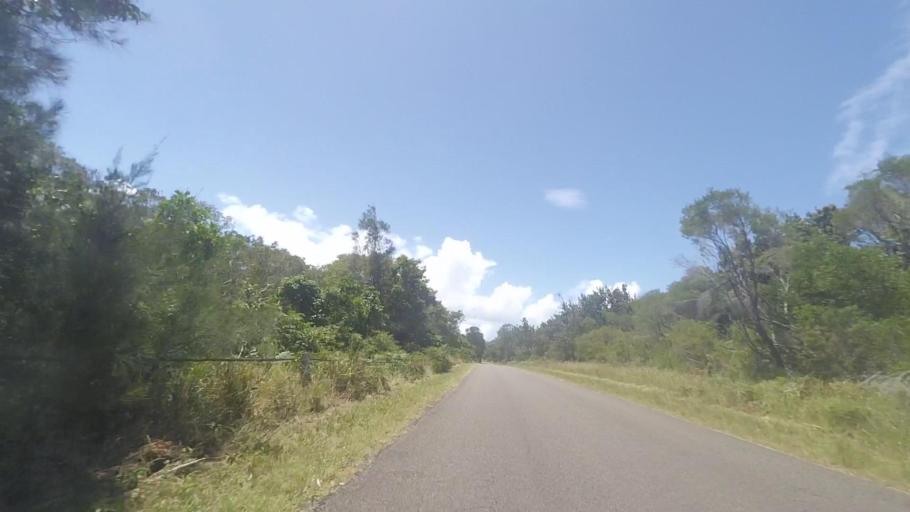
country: AU
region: New South Wales
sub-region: Great Lakes
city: Bulahdelah
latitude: -32.5365
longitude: 152.3194
